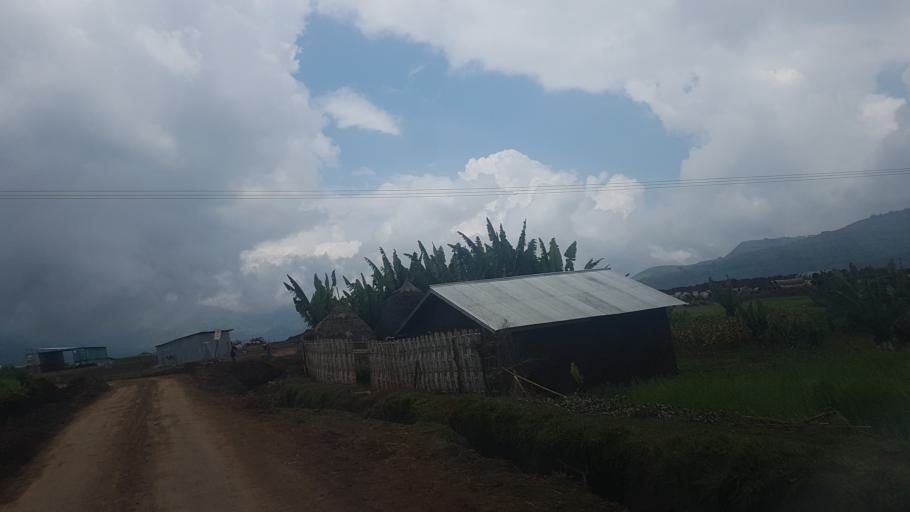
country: ET
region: Southern Nations, Nationalities, and People's Region
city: Arba Minch'
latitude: 6.3257
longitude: 37.5429
